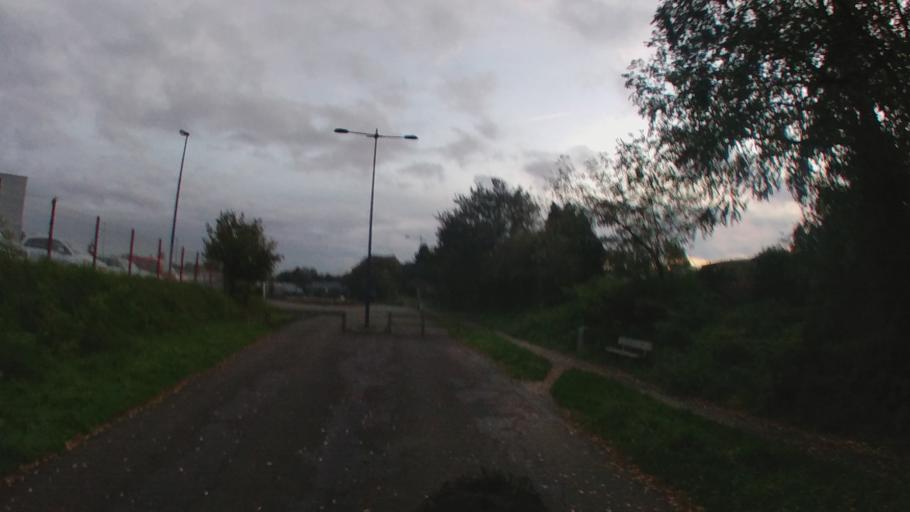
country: FR
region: Pays de la Loire
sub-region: Departement de la Mayenne
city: Mayenne
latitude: 48.2945
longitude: -0.6138
